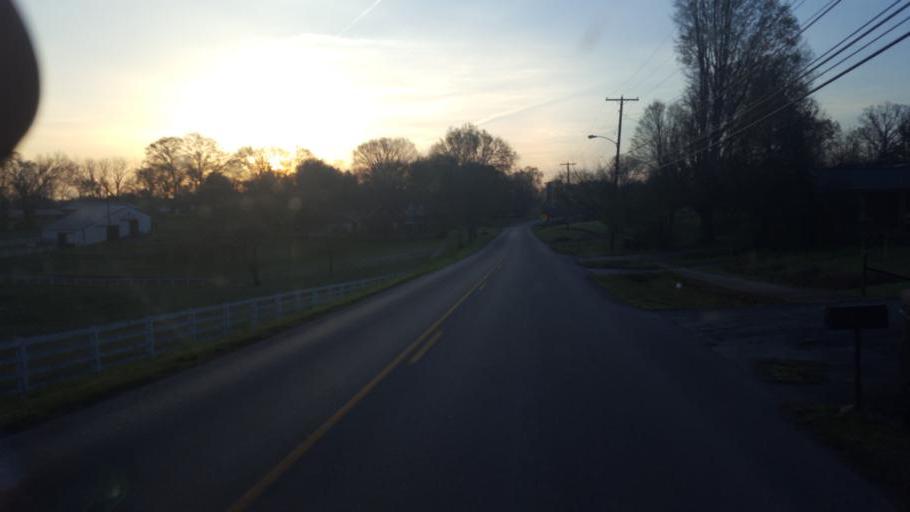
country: US
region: Kentucky
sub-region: Hart County
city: Munfordville
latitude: 37.2730
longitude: -85.8993
